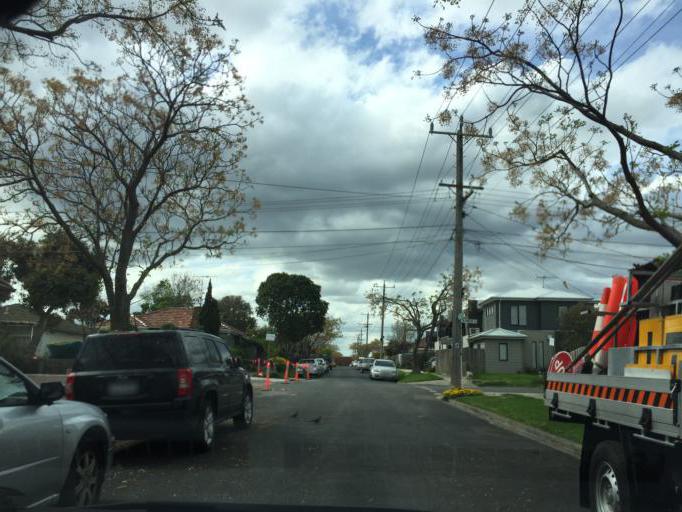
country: AU
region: Victoria
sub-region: Maribyrnong
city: West Footscray
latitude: -37.8027
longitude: 144.8648
